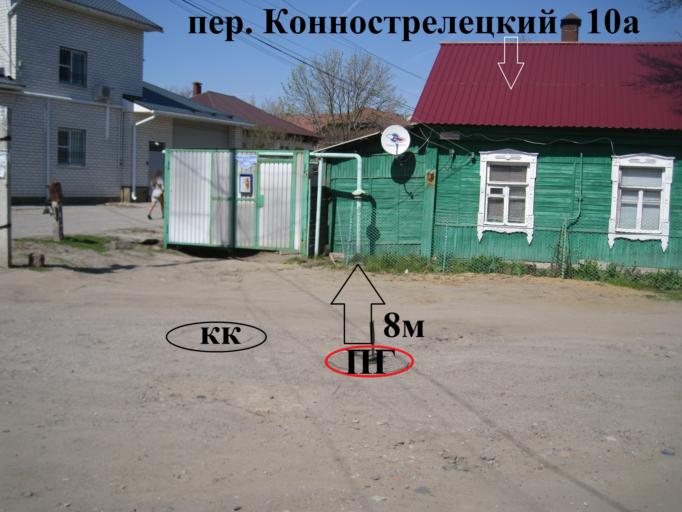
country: RU
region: Voronezj
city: Voronezh
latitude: 51.6494
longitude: 39.1829
